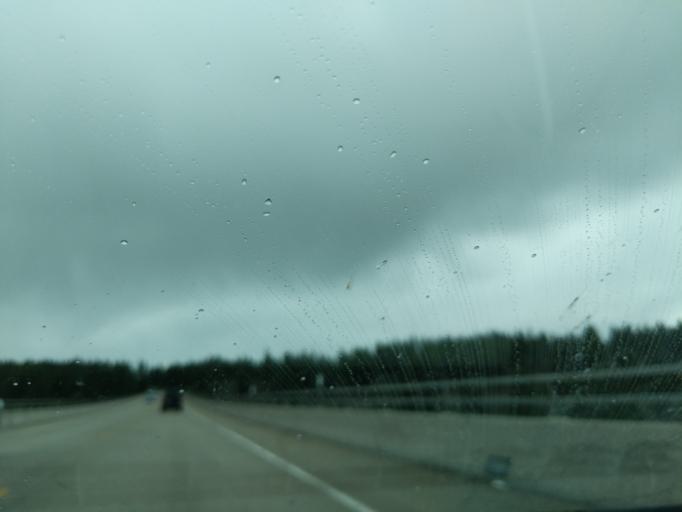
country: US
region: California
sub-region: Nevada County
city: Truckee
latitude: 39.3307
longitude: -120.1609
